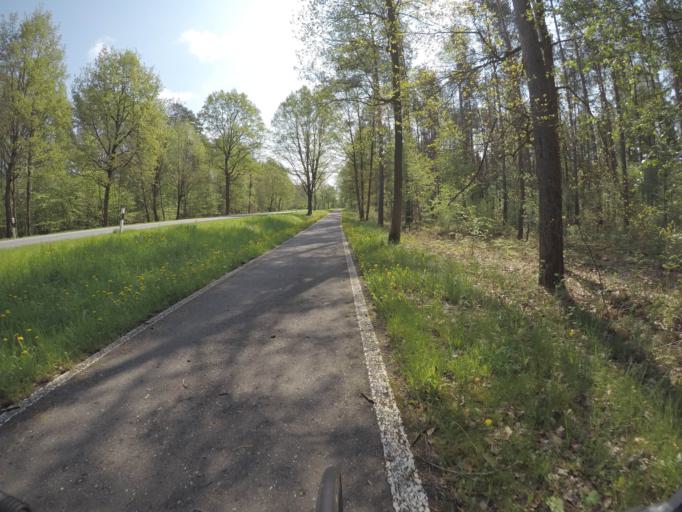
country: DE
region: Brandenburg
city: Wandlitz
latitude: 52.7942
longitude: 13.5245
